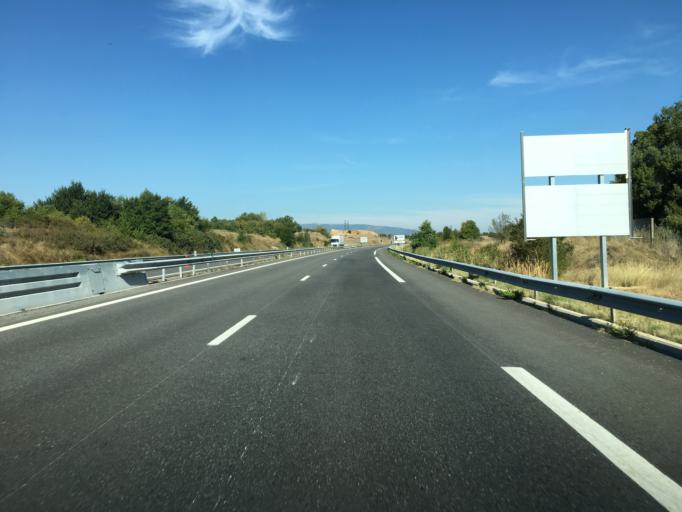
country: FR
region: Provence-Alpes-Cote d'Azur
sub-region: Departement des Alpes-de-Haute-Provence
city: Sisteron
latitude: 44.2055
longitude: 5.9407
